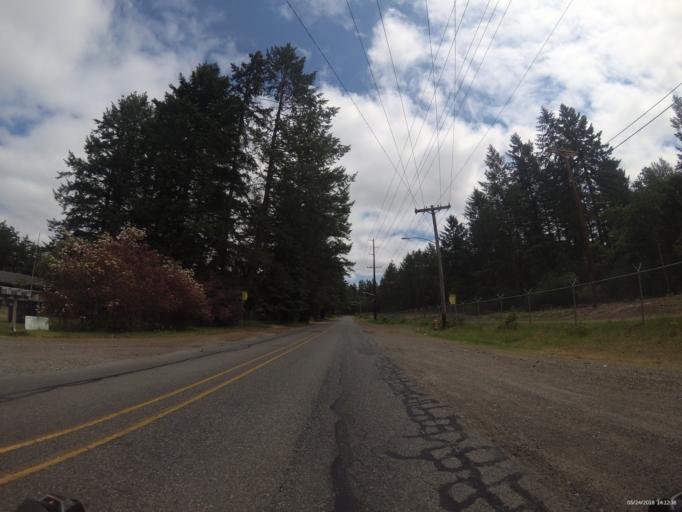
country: US
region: Washington
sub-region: Pierce County
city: McChord Air Force Base
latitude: 47.1403
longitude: -122.5129
